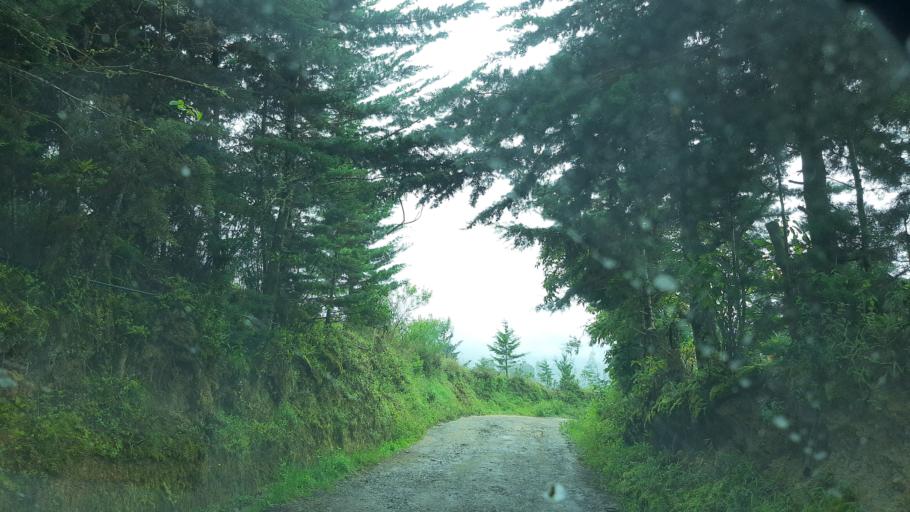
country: CO
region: Cundinamarca
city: Tenza
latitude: 5.0427
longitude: -73.4300
